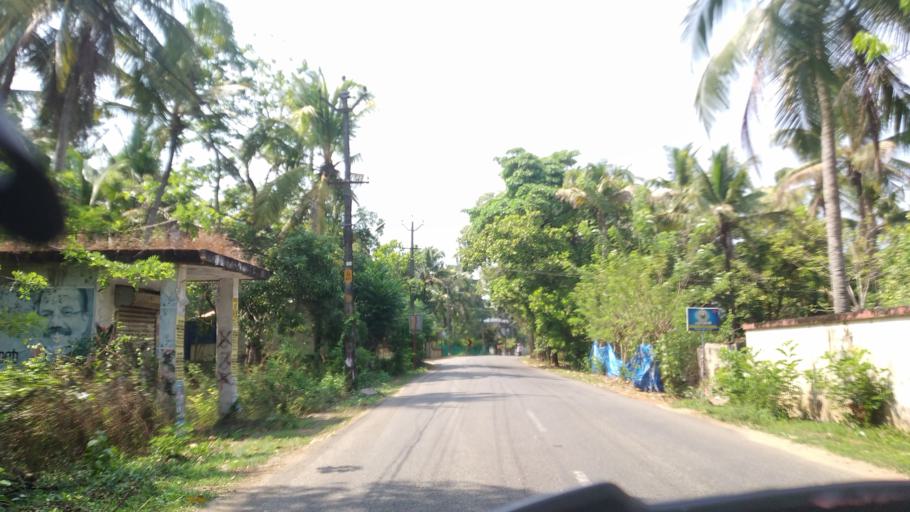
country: IN
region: Kerala
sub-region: Thrissur District
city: Irinjalakuda
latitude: 10.2936
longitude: 76.1338
